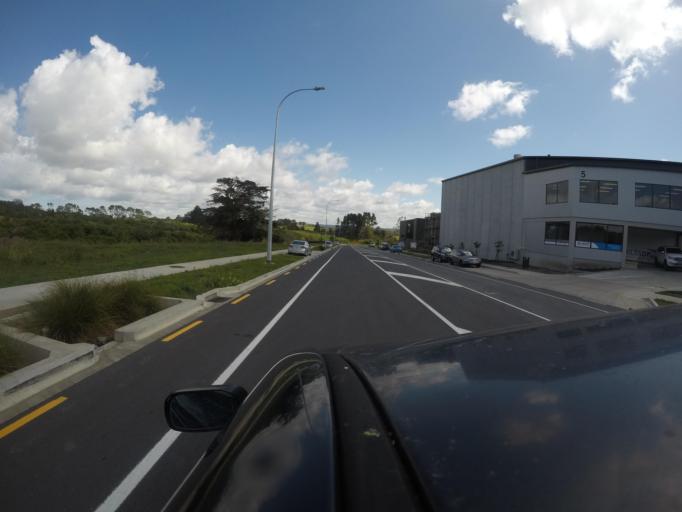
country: NZ
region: Auckland
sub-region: Auckland
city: Rosebank
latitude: -36.8117
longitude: 174.6307
